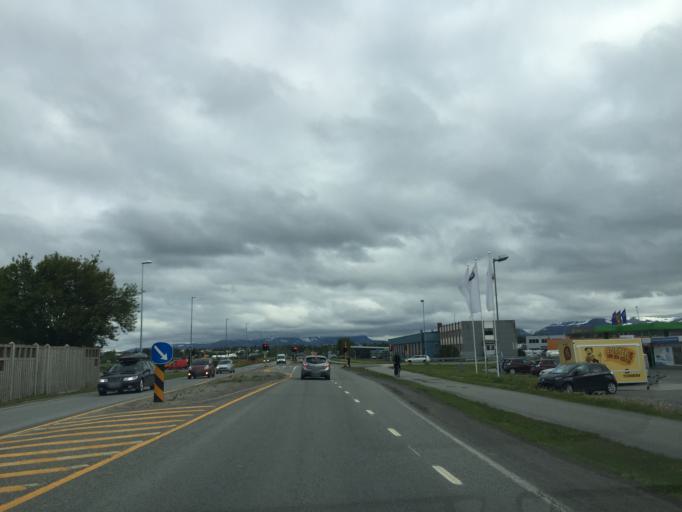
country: NO
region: Nordland
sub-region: Bodo
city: Bodo
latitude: 67.2834
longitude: 14.4126
